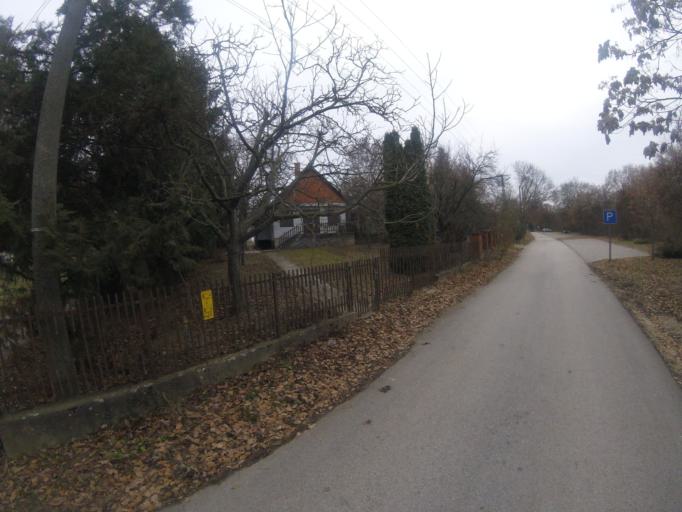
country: HU
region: Somogy
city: Balatonfoldvar
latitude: 46.8428
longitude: 17.8770
